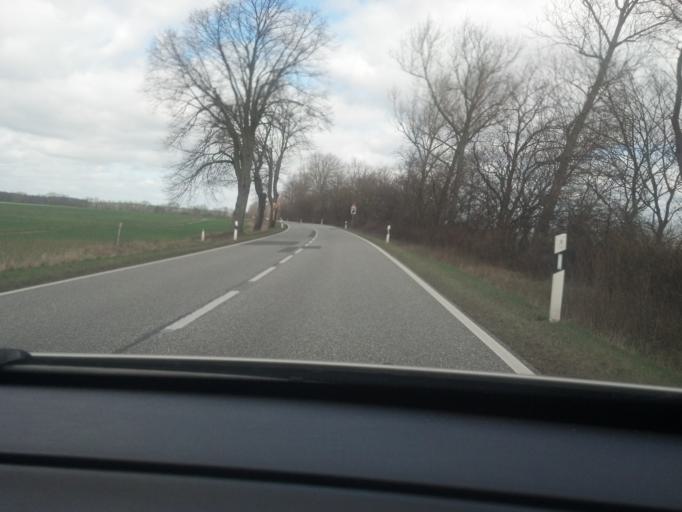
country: DE
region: Brandenburg
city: Gerdshagen
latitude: 53.3345
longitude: 12.2462
